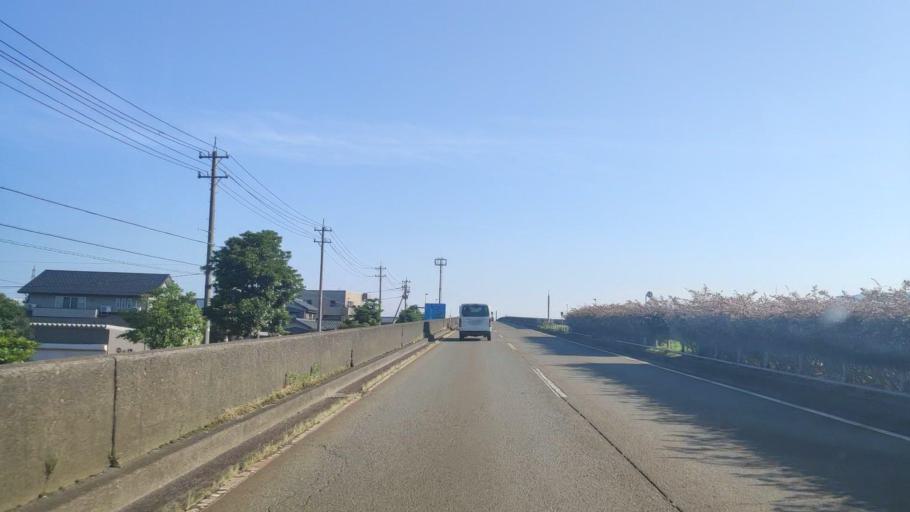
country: JP
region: Fukui
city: Maruoka
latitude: 36.1411
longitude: 136.2637
